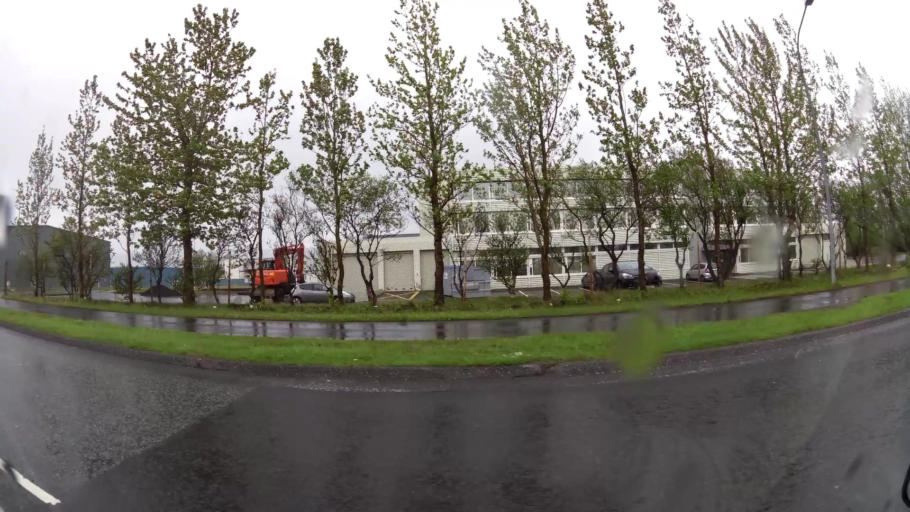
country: IS
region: Capital Region
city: Mosfellsbaer
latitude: 64.1171
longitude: -21.7876
